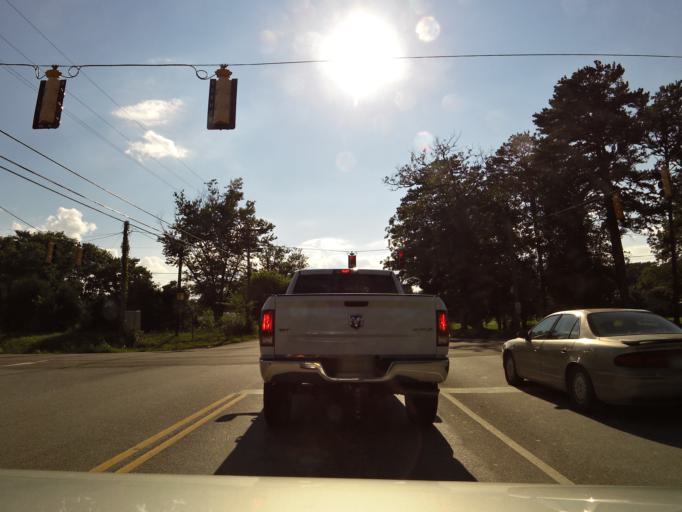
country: US
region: Tennessee
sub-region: Blount County
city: Maryville
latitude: 35.7448
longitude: -84.0441
